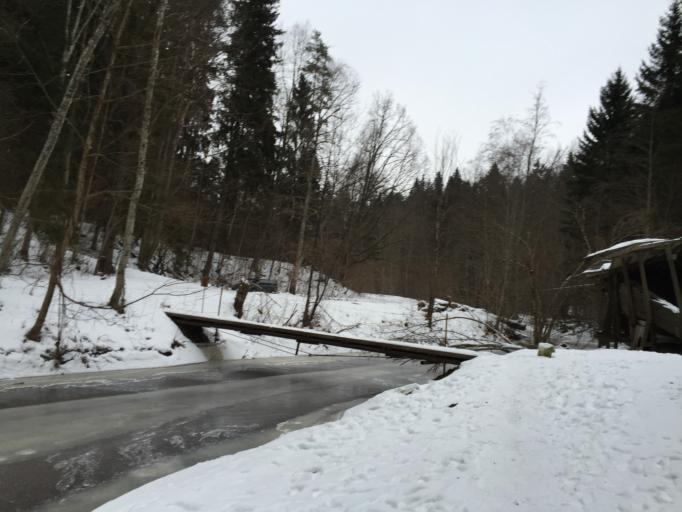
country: LV
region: Seja
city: Loja
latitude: 57.1442
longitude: 24.6808
